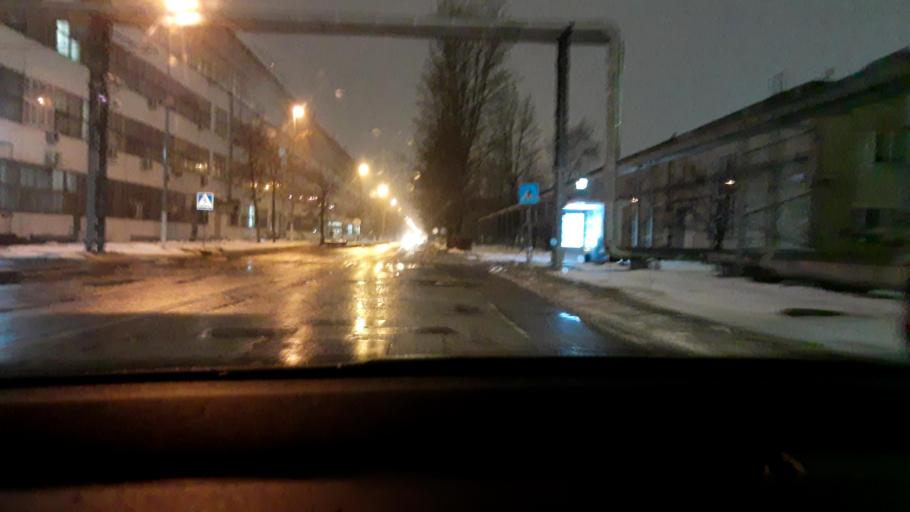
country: RU
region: Moskovskaya
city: Yakovlevskoye
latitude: 55.4180
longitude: 37.8893
